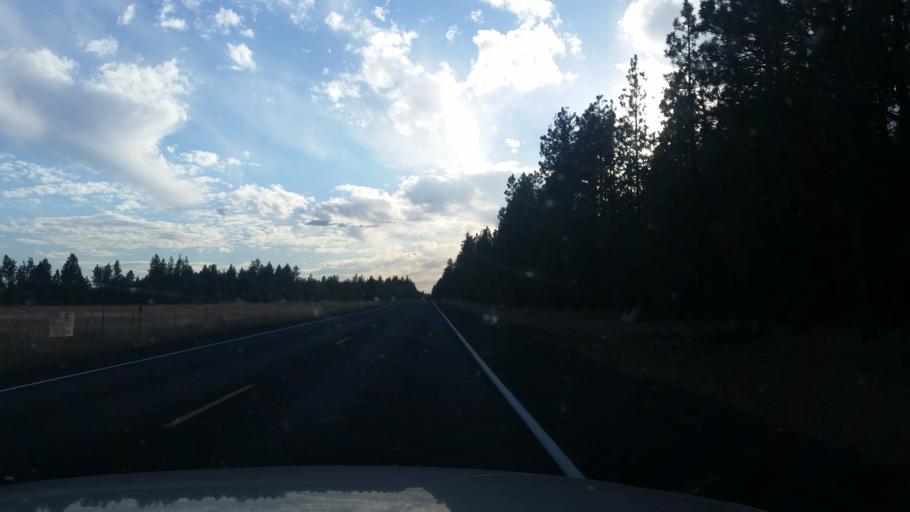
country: US
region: Washington
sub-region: Spokane County
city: Cheney
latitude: 47.4625
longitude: -117.6780
